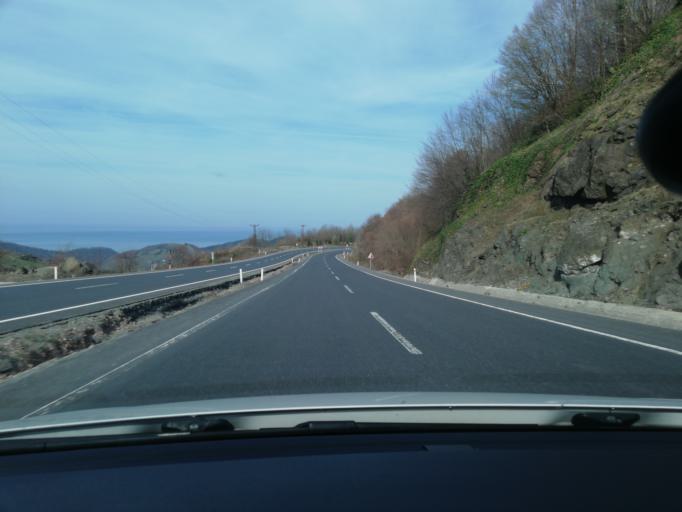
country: TR
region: Zonguldak
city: Eregli
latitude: 41.3292
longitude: 31.5729
